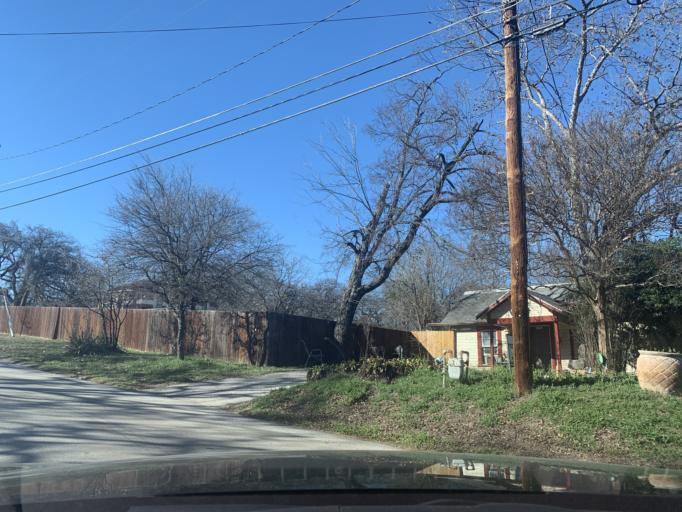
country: US
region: Texas
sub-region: Tarrant County
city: Haltom City
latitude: 32.7816
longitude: -97.2795
